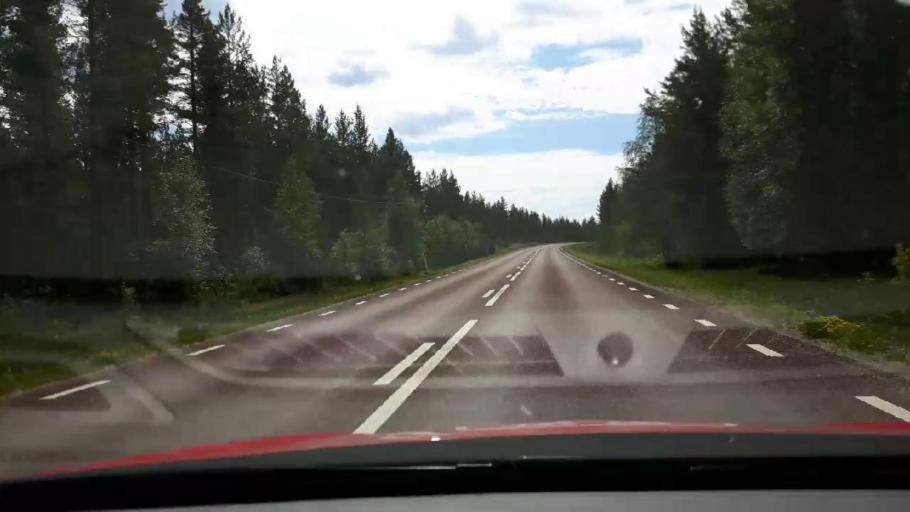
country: SE
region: Jaemtland
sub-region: Harjedalens Kommun
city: Sveg
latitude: 62.1081
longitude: 14.9710
